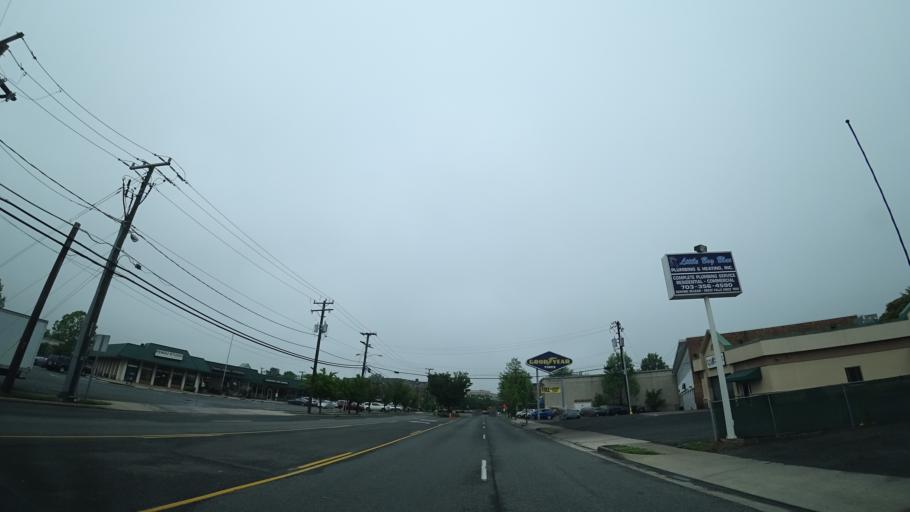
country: US
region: Virginia
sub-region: Fairfax County
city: McLean
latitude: 38.9344
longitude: -77.1783
